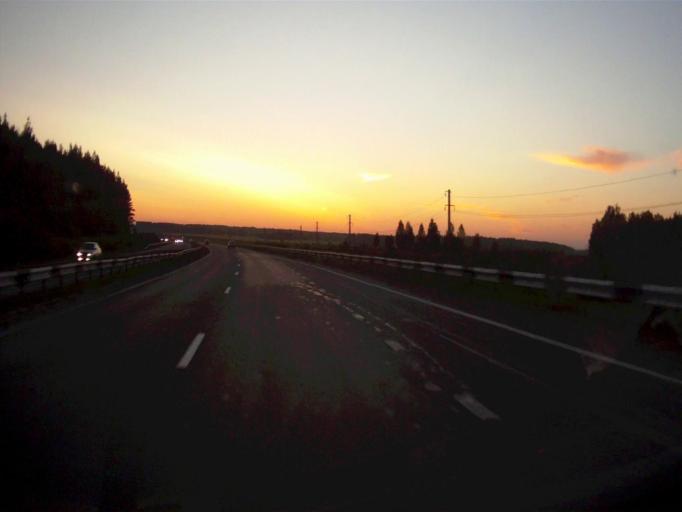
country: RU
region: Chelyabinsk
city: Roshchino
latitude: 55.1943
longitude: 61.2135
